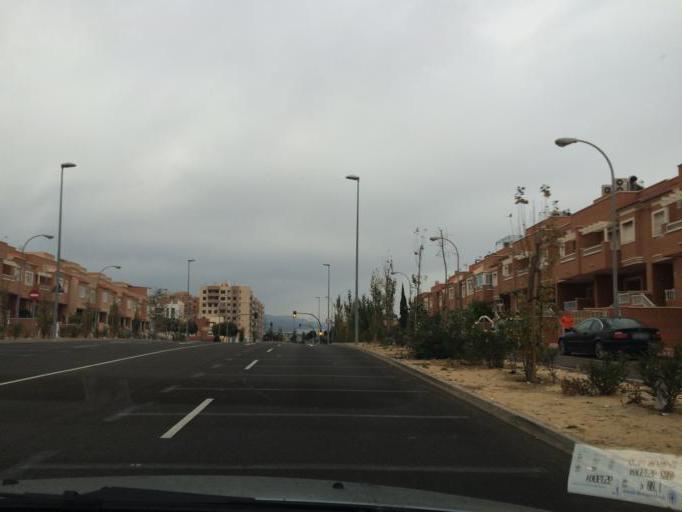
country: ES
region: Andalusia
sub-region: Provincia de Almeria
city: Almeria
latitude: 36.8571
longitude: -2.4439
